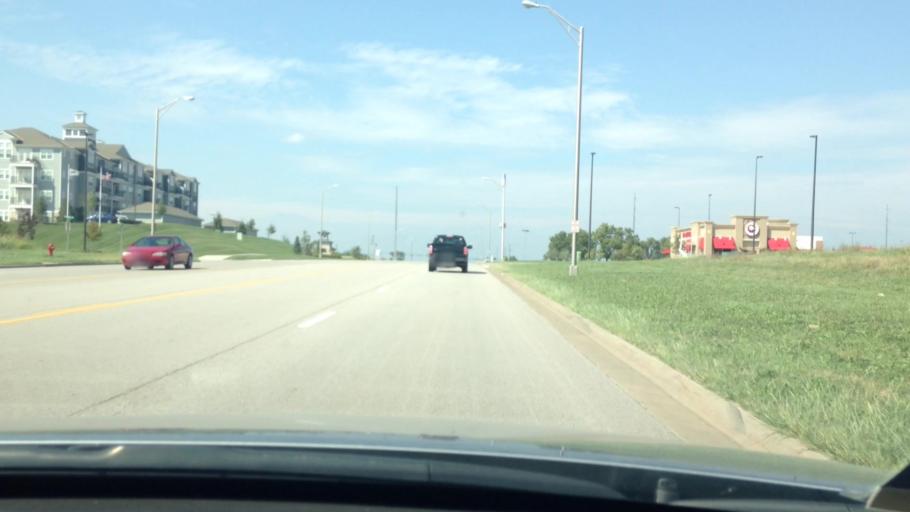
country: US
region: Kansas
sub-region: Wyandotte County
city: Edwardsville
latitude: 39.1247
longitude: -94.8351
